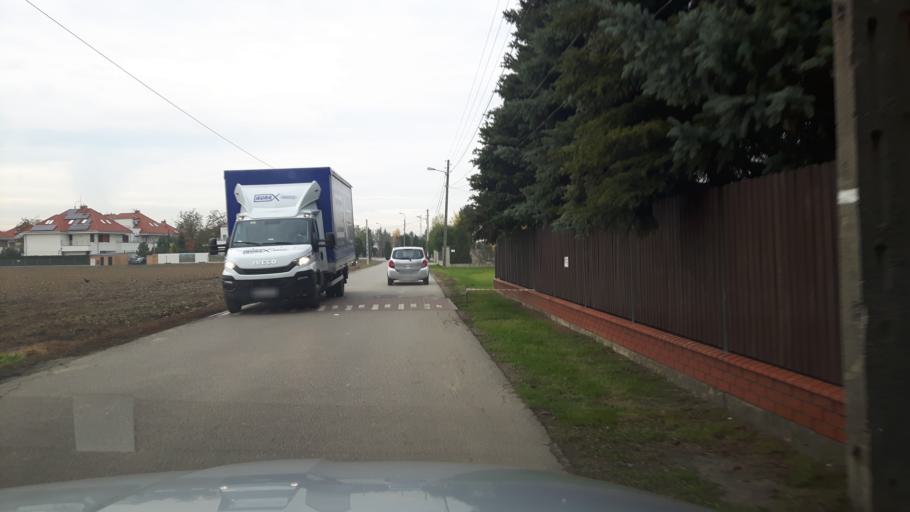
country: PL
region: Masovian Voivodeship
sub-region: Warszawa
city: Wilanow
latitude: 52.1621
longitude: 21.1241
